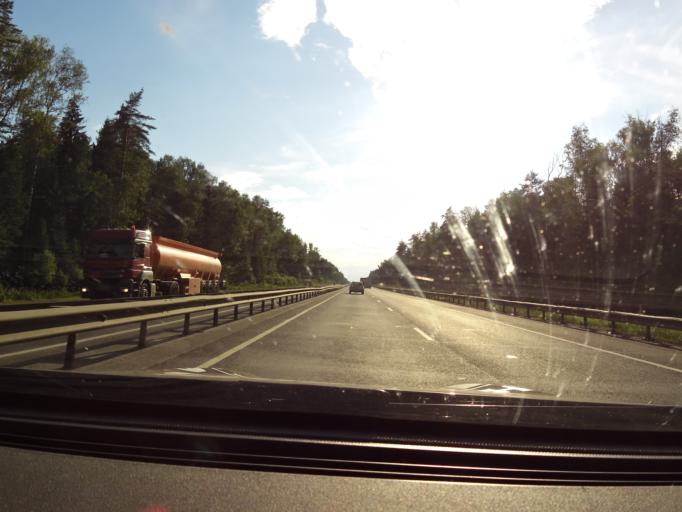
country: RU
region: Vladimir
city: Krasnyy Oktyabr'
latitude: 56.2155
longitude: 41.3999
